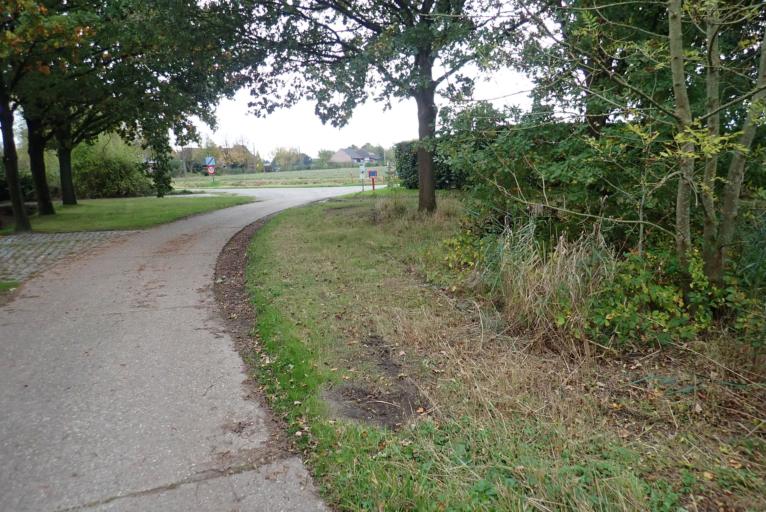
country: BE
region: Flanders
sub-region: Provincie Antwerpen
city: Kalmthout
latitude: 51.4098
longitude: 4.4782
